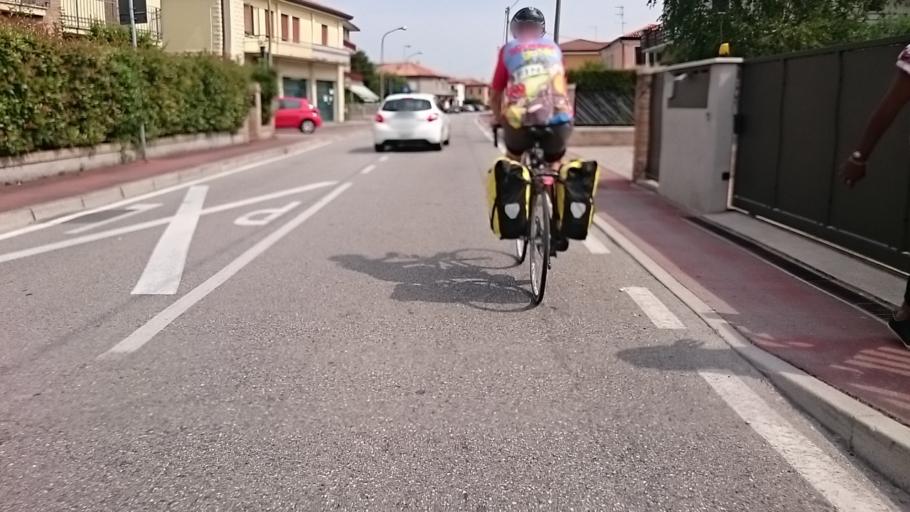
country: IT
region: Veneto
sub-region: Provincia di Venezia
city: Fornase
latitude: 45.4563
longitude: 12.1736
